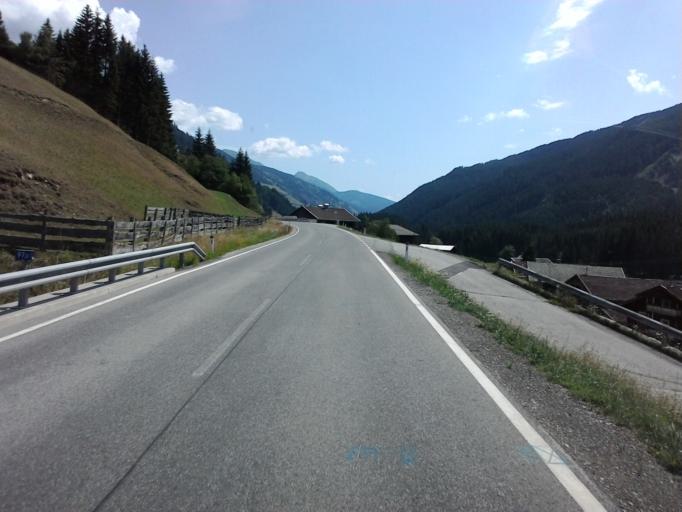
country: AT
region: Tyrol
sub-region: Politischer Bezirk Lienz
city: Untertilliach
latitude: 46.7016
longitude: 12.6646
